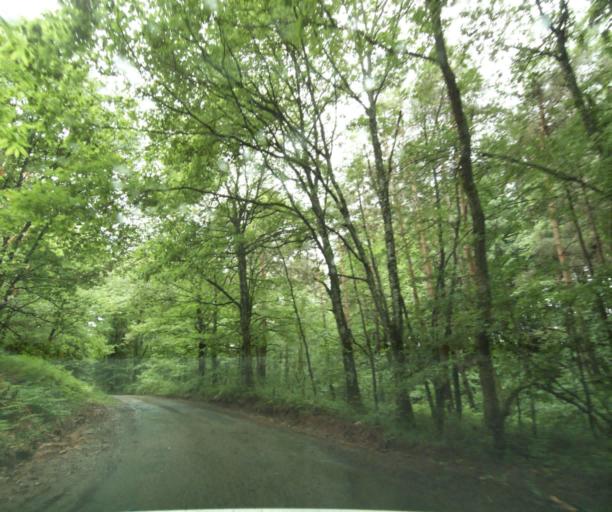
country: FR
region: Bourgogne
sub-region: Departement de Saone-et-Loire
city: Matour
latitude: 46.4512
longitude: 4.4646
